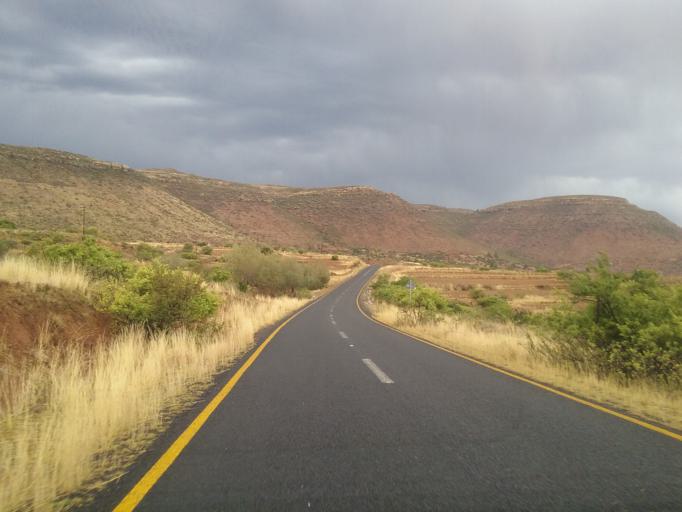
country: LS
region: Quthing
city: Quthing
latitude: -30.3453
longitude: 27.7187
